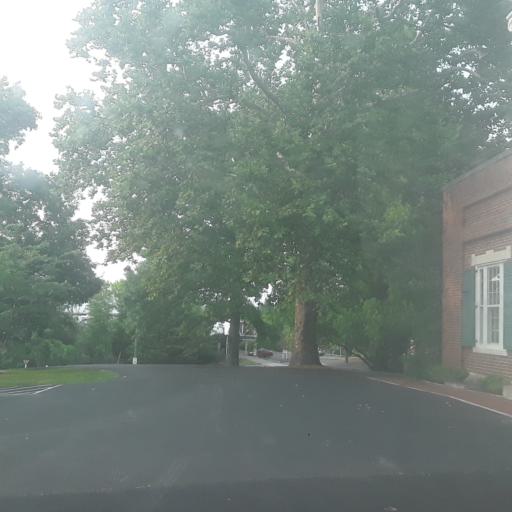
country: US
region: Tennessee
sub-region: Davidson County
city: Oak Hill
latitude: 36.0638
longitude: -86.7475
